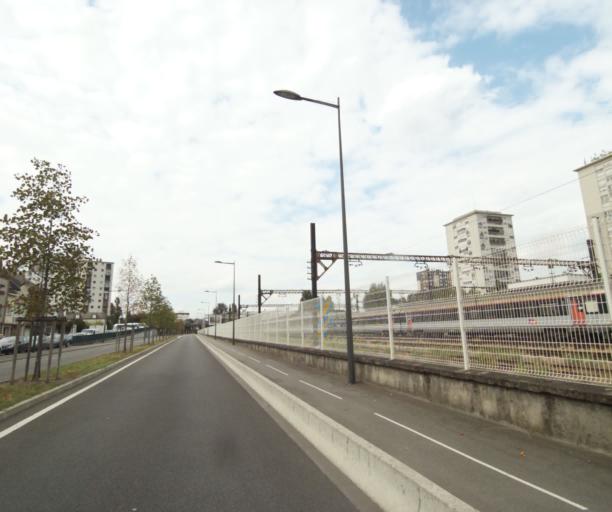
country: FR
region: Centre
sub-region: Departement du Loiret
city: Orleans
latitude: 47.9123
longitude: 1.9046
